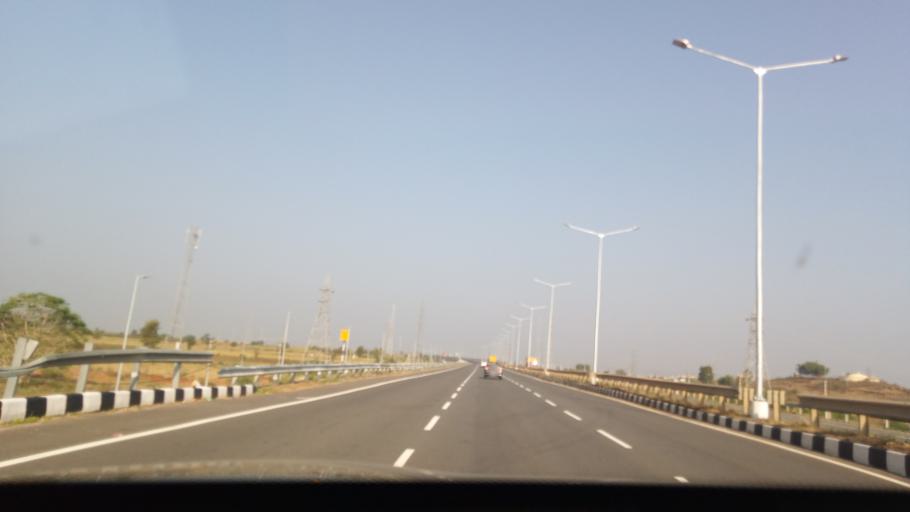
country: IN
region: Karnataka
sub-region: Haveri
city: Ranibennur
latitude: 14.6036
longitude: 75.6220
